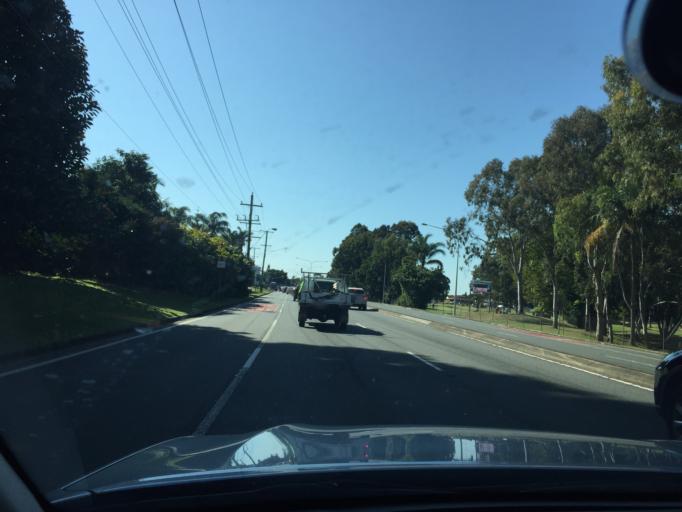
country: AU
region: Queensland
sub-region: Gold Coast
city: Clear Island Waters
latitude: -28.0317
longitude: 153.4001
